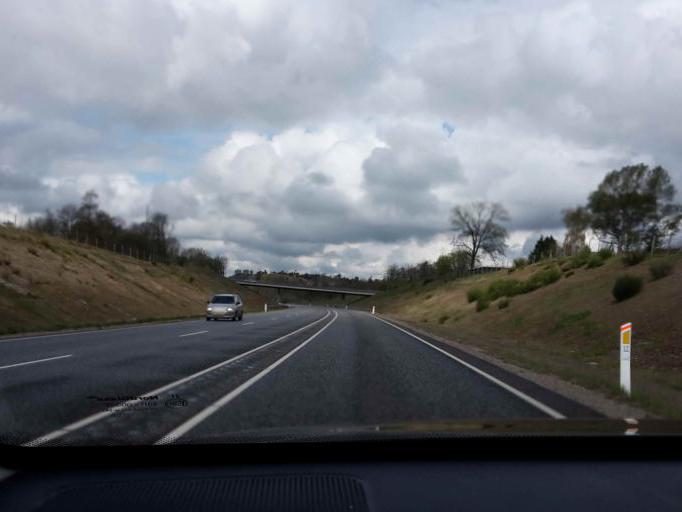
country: DK
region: South Denmark
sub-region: Vejle Kommune
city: Egtved
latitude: 55.7044
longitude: 9.2890
